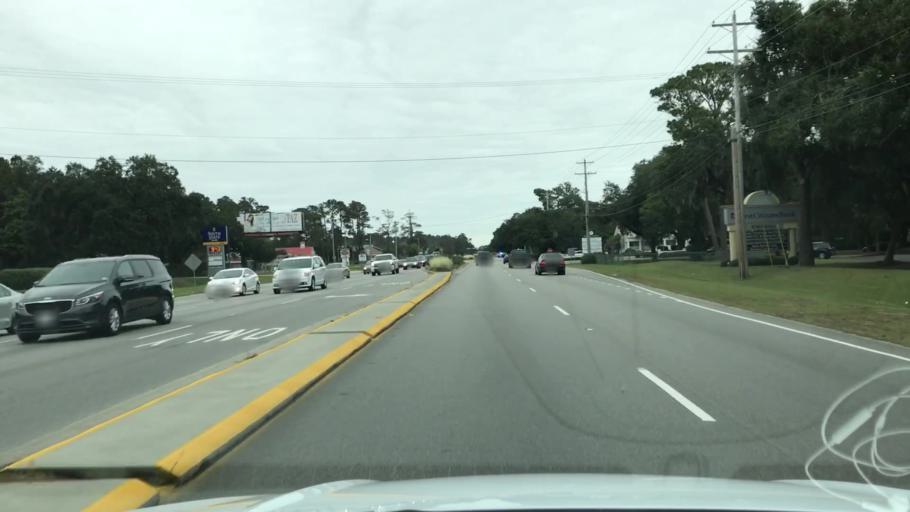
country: US
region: South Carolina
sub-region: Georgetown County
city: Murrells Inlet
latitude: 33.4450
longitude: -79.1226
